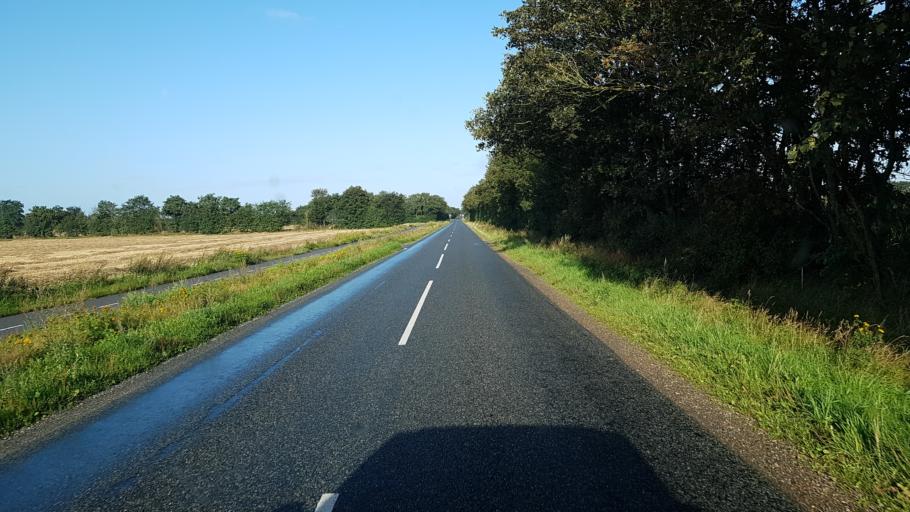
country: DK
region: South Denmark
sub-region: Esbjerg Kommune
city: Bramming
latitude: 55.4823
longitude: 8.7676
